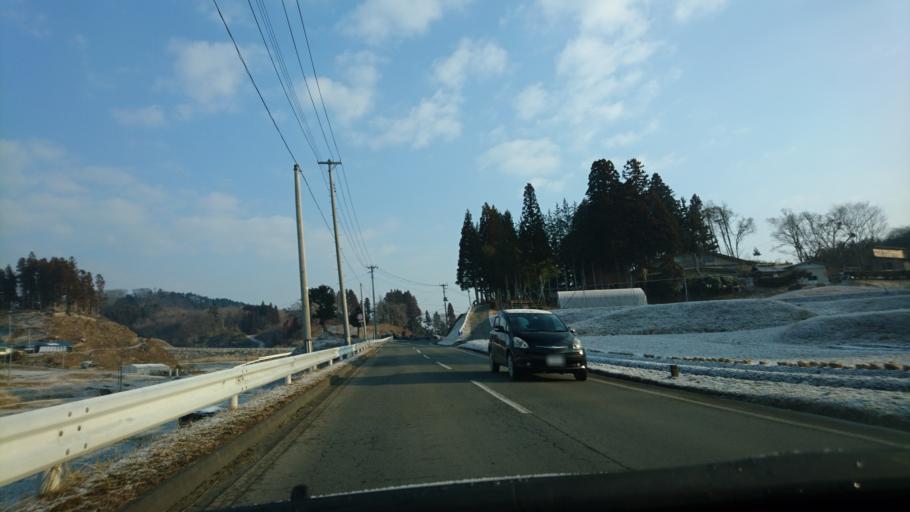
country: JP
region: Iwate
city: Ichinoseki
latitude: 38.9099
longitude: 141.3777
